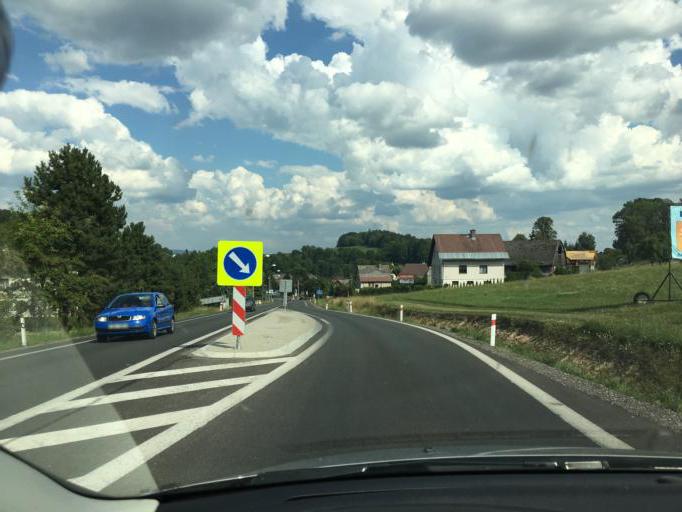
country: CZ
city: Horni Branna
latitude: 50.6215
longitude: 15.5539
